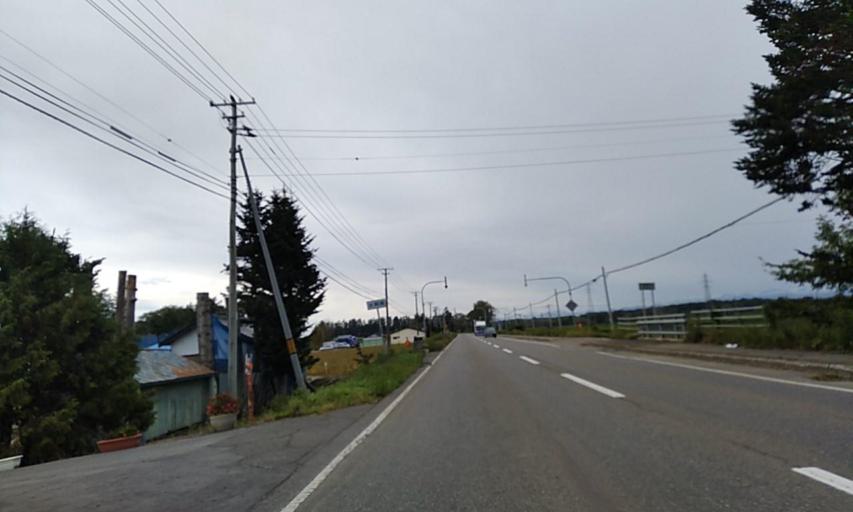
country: JP
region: Hokkaido
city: Obihiro
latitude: 42.7717
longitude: 143.1533
